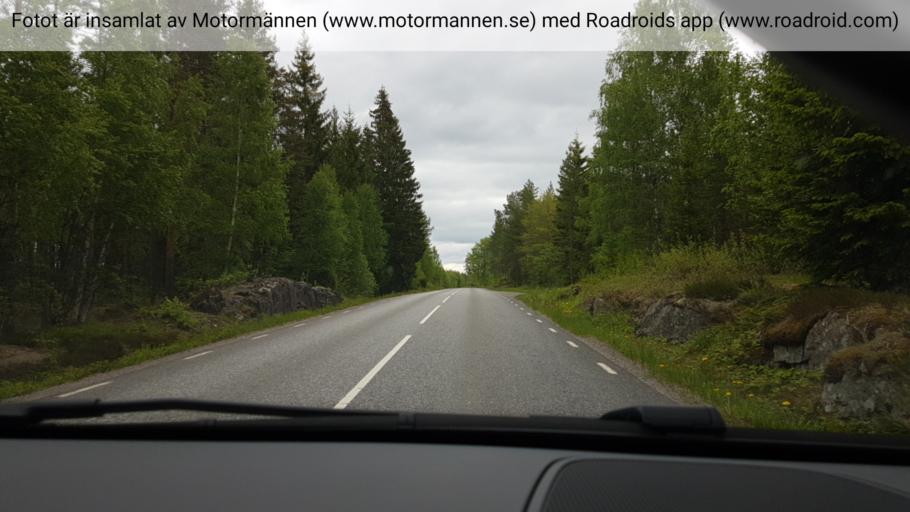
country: SE
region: Uppsala
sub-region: Heby Kommun
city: OEstervala
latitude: 60.0883
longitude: 17.0777
